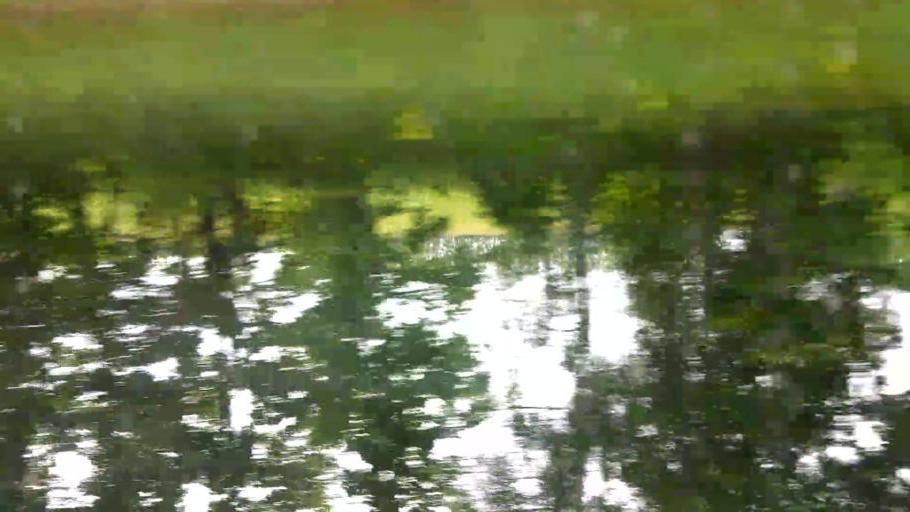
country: RU
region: Moskovskaya
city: Ozherel'ye
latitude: 54.8432
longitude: 38.2699
